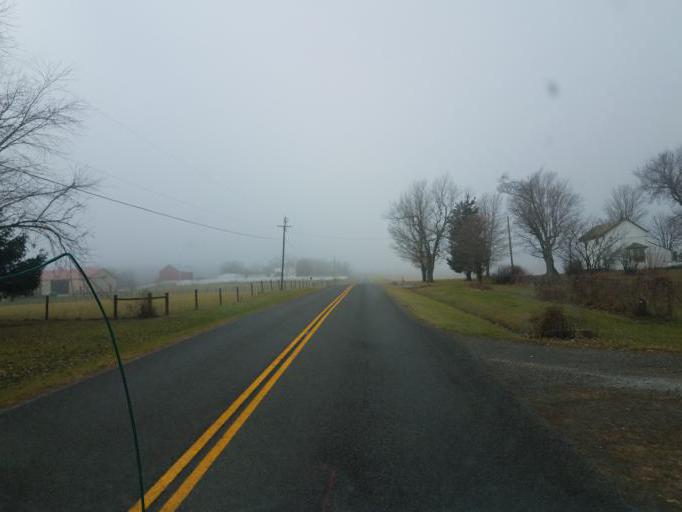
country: US
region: Ohio
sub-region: Champaign County
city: North Lewisburg
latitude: 40.3027
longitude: -83.6048
